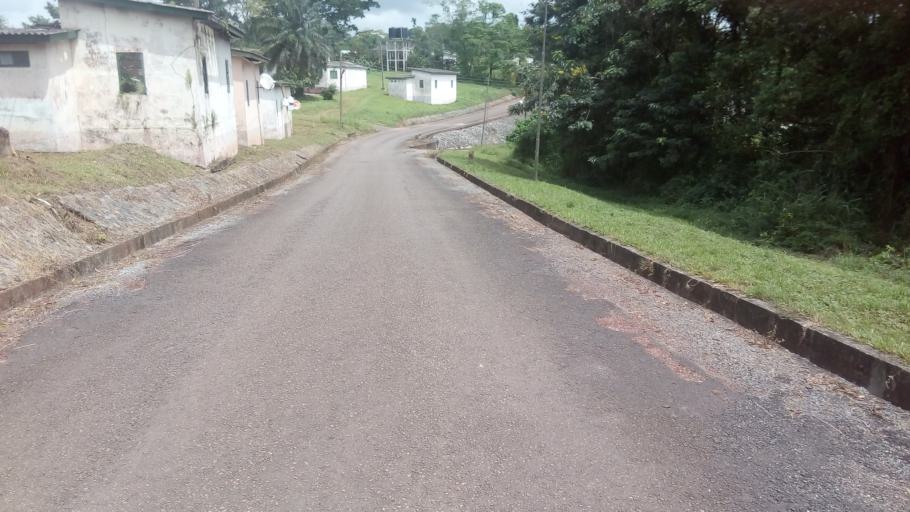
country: GH
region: Western
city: Tarkwa
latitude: 5.2934
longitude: -2.0090
